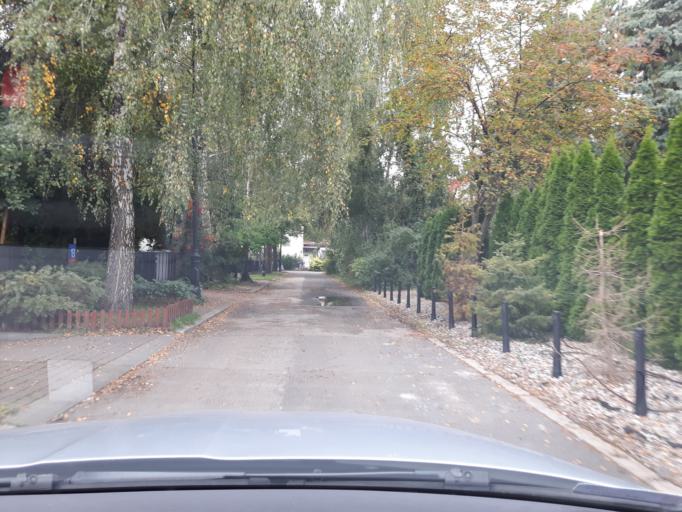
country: PL
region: Masovian Voivodeship
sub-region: Warszawa
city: Mokotow
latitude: 52.1857
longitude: 21.0336
